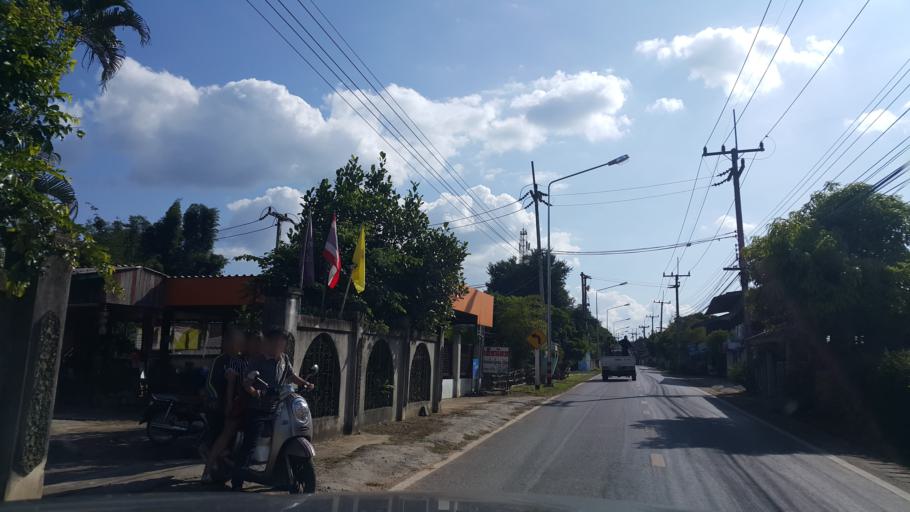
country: TH
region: Lamphun
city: Mae Tha
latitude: 18.5491
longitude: 99.2454
